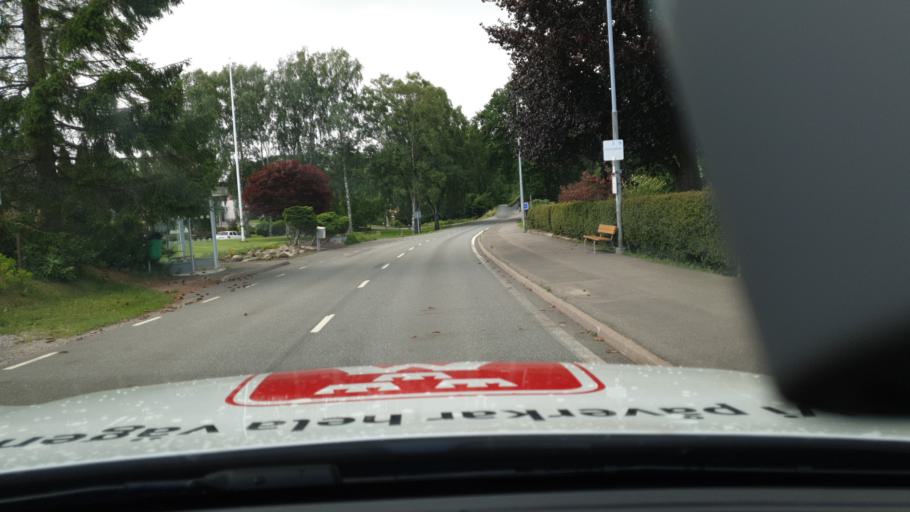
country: SE
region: Vaestra Goetaland
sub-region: Falkopings Kommun
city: Akarp
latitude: 58.2103
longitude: 13.6054
